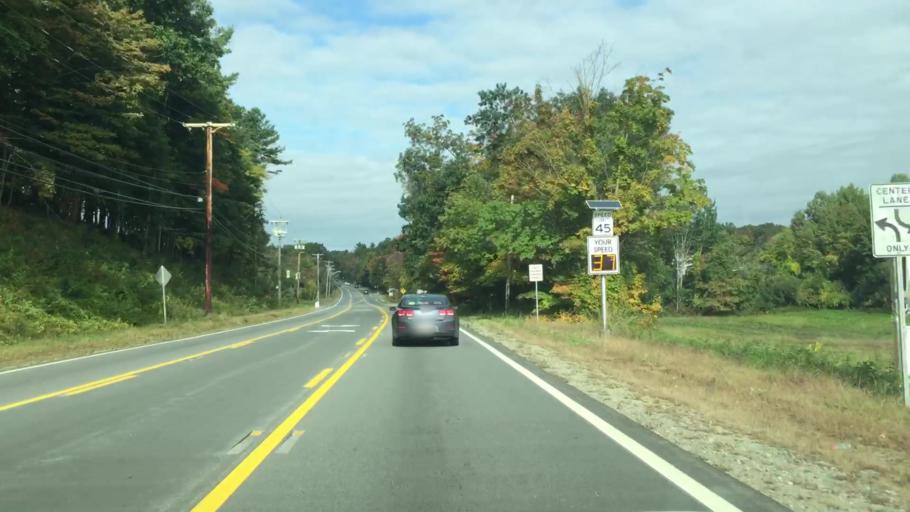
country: US
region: Massachusetts
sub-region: Essex County
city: Andover
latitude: 42.6474
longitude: -71.0904
